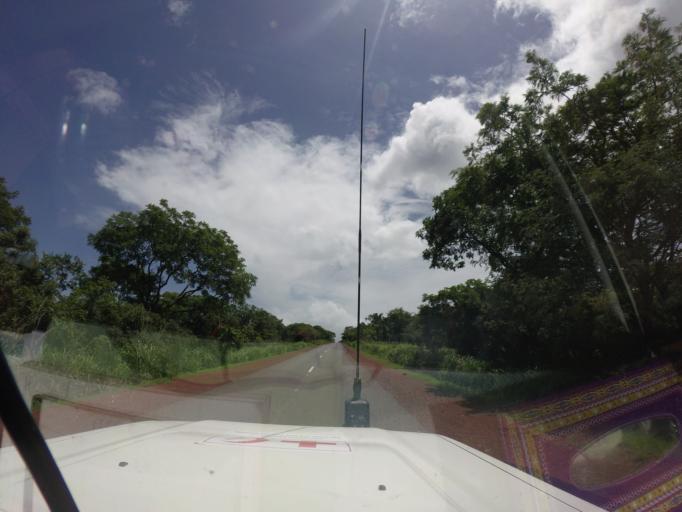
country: GN
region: Faranah
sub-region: Faranah Prefecture
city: Faranah
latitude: 10.0146
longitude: -10.8431
